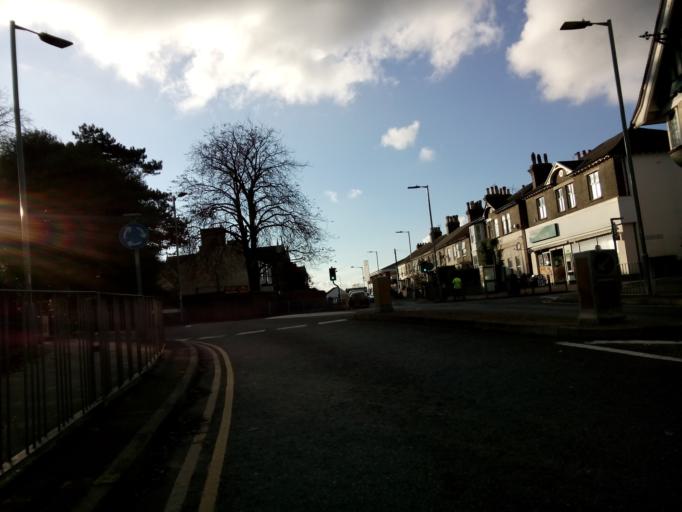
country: GB
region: England
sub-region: Suffolk
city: Ipswich
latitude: 52.0615
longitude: 1.1751
